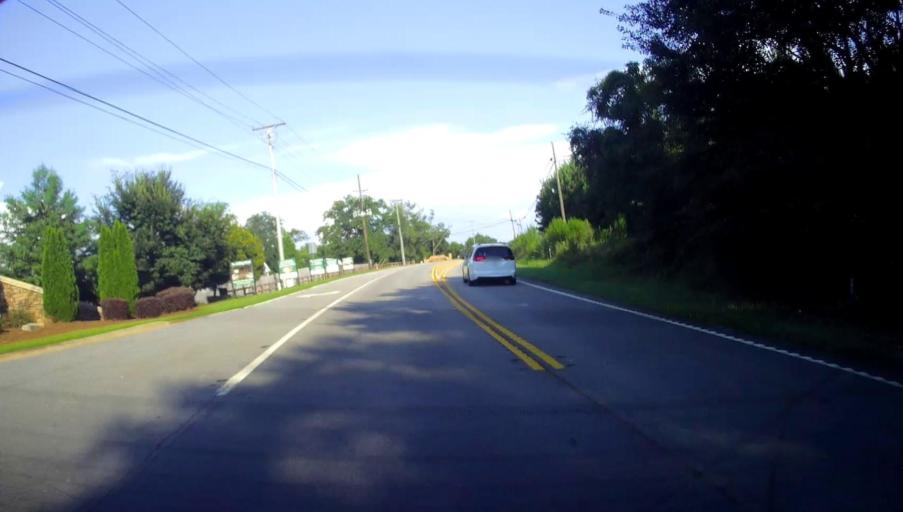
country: US
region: Georgia
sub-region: Houston County
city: Perry
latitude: 32.5060
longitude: -83.6408
